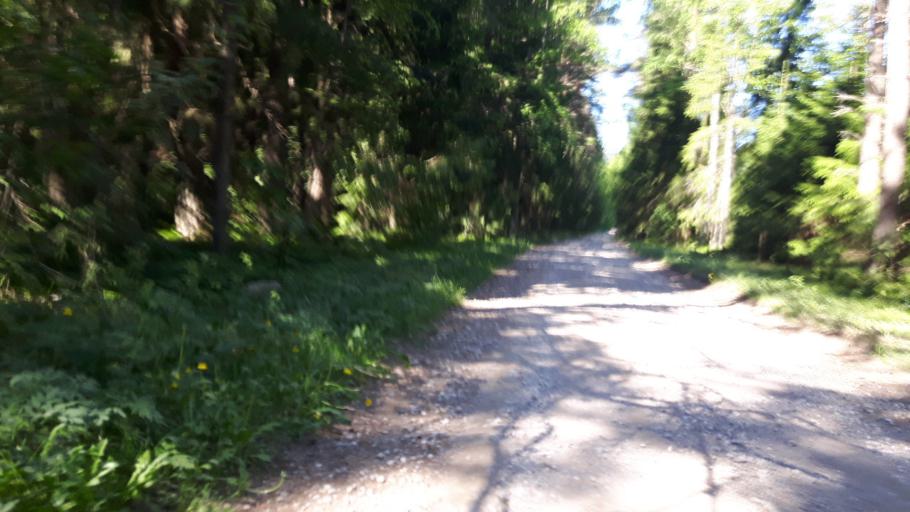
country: EE
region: Harju
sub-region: Loksa linn
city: Loksa
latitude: 59.5585
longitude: 25.8049
